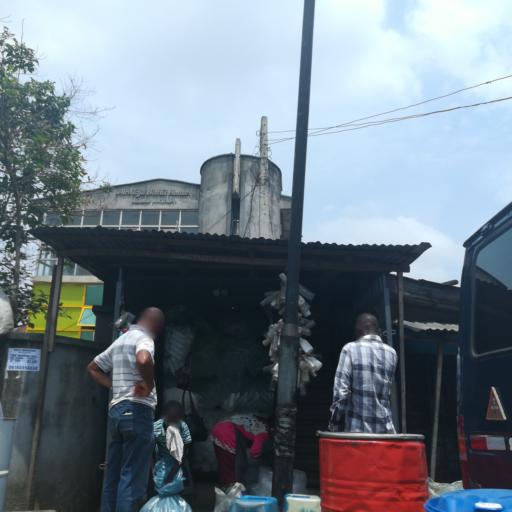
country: NG
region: Lagos
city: Ojota
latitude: 6.5874
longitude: 3.3801
